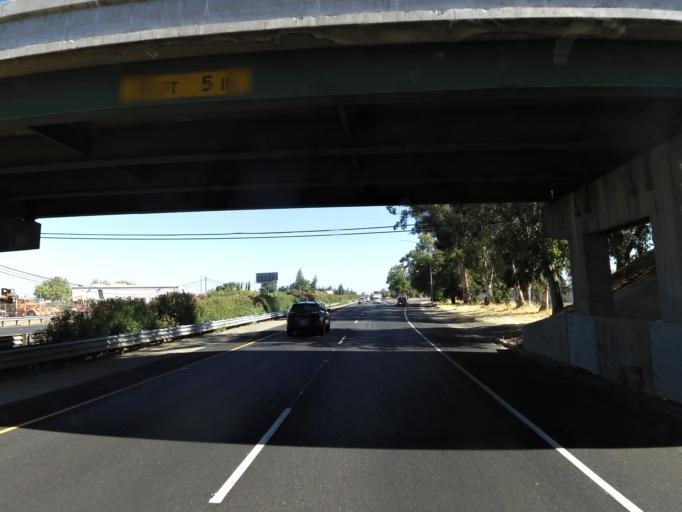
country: US
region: California
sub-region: San Joaquin County
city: Lodi
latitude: 38.1600
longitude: -121.2616
